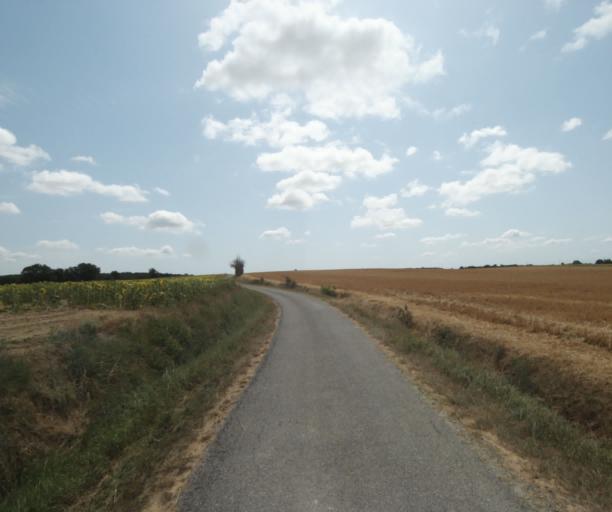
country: FR
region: Midi-Pyrenees
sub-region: Departement de la Haute-Garonne
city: Saint-Felix-Lauragais
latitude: 43.4030
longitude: 1.9033
